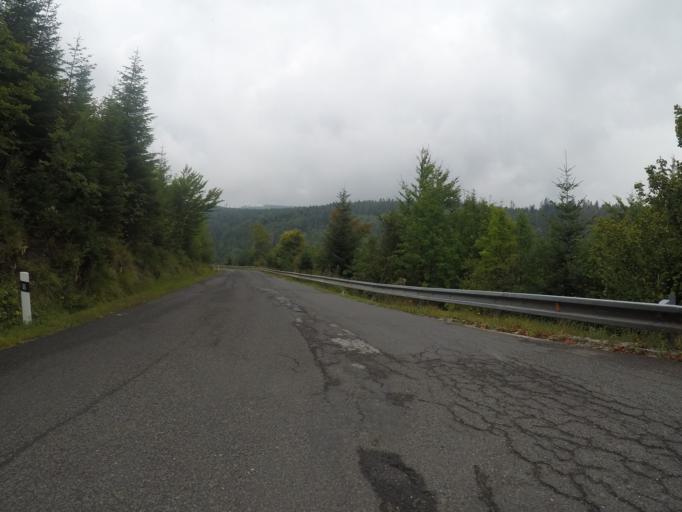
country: SK
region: Kosicky
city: Spisska Nova Ves
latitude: 48.8700
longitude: 20.5262
